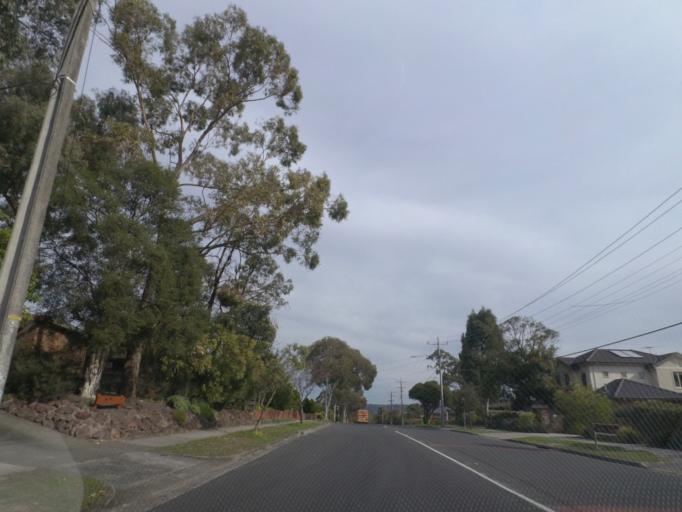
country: AU
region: Victoria
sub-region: Whitehorse
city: Vermont
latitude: -37.8477
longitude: 145.1969
